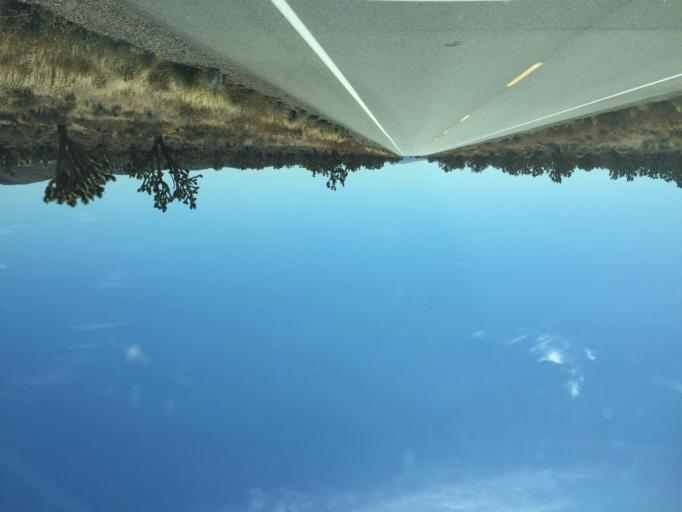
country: US
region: Arizona
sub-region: Mohave County
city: Meadview
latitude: 35.8711
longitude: -114.0638
